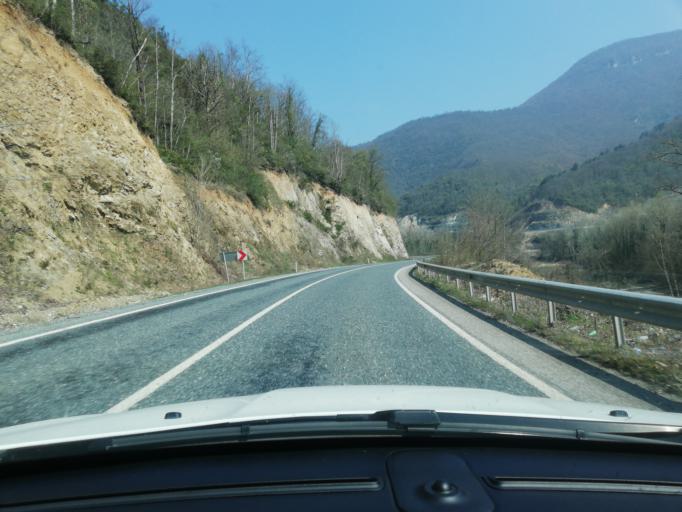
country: TR
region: Zonguldak
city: Gokcebey
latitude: 41.2497
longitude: 32.1660
